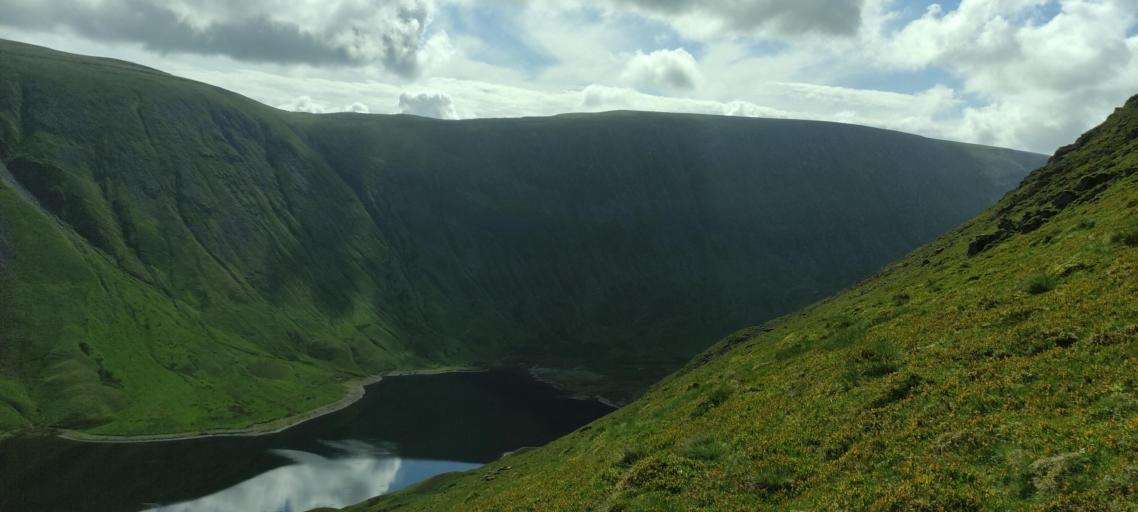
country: GB
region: England
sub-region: Cumbria
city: Ambleside
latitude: 54.5024
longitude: -2.8895
